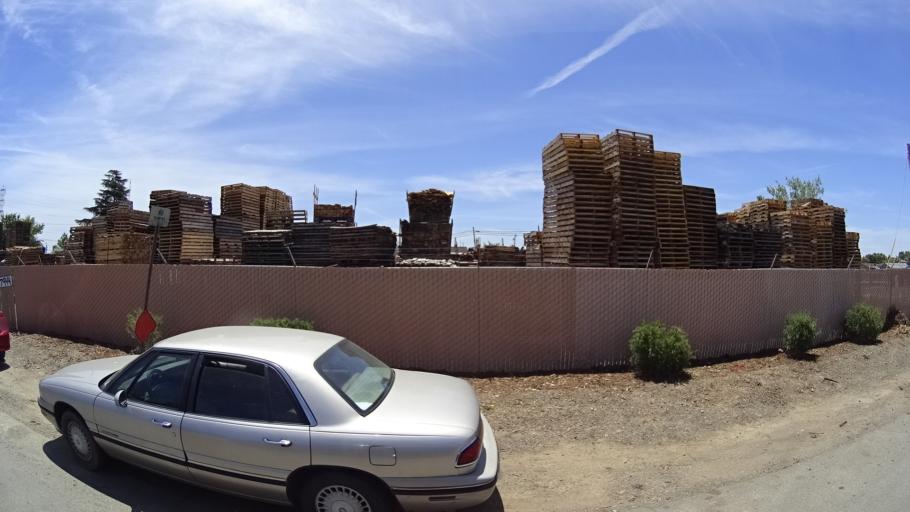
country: US
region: California
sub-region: Sacramento County
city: Florin
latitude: 38.5359
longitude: -121.4105
